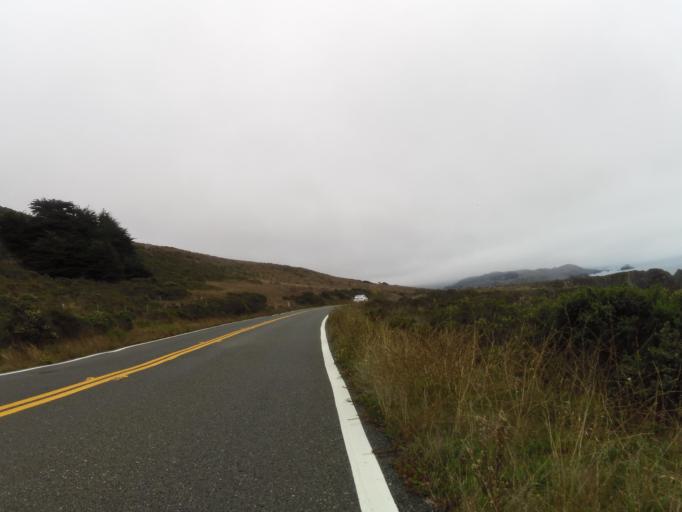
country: US
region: California
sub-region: Sonoma County
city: Monte Rio
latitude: 38.4625
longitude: -123.1470
